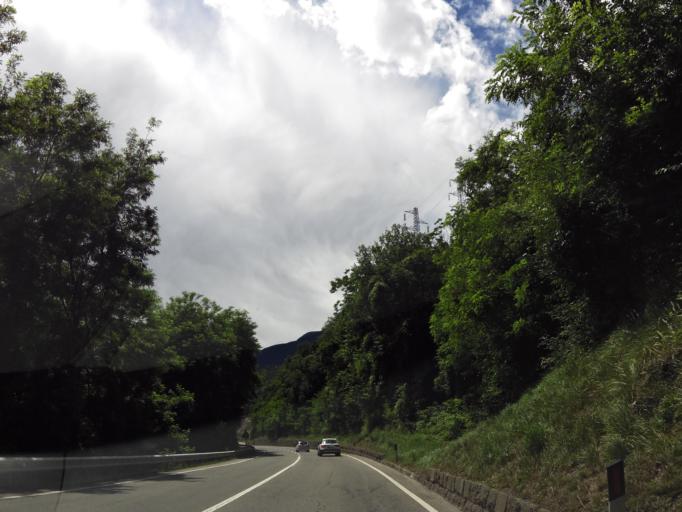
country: IT
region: Trentino-Alto Adige
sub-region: Bolzano
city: Villandro
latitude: 46.6250
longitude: 11.5462
